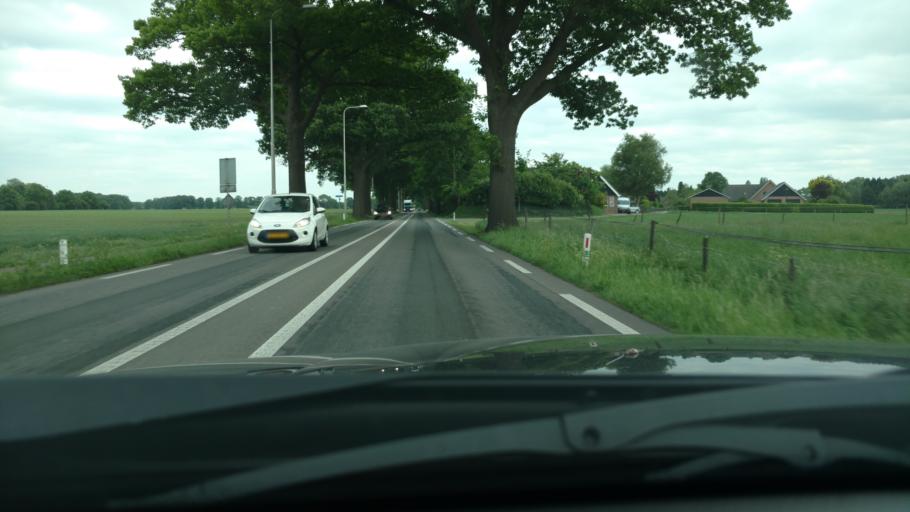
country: NL
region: Gelderland
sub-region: Gemeente Lochem
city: Epse
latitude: 52.2238
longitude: 6.1935
